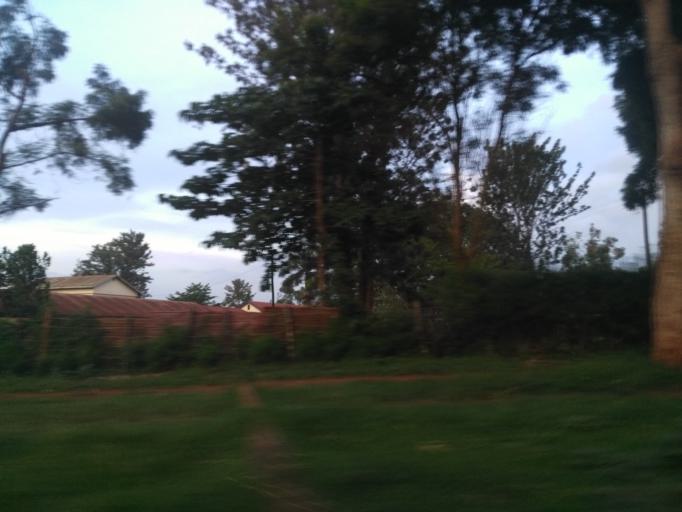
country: UG
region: Eastern Region
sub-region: Jinja District
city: Jinja
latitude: 0.4261
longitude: 33.2015
